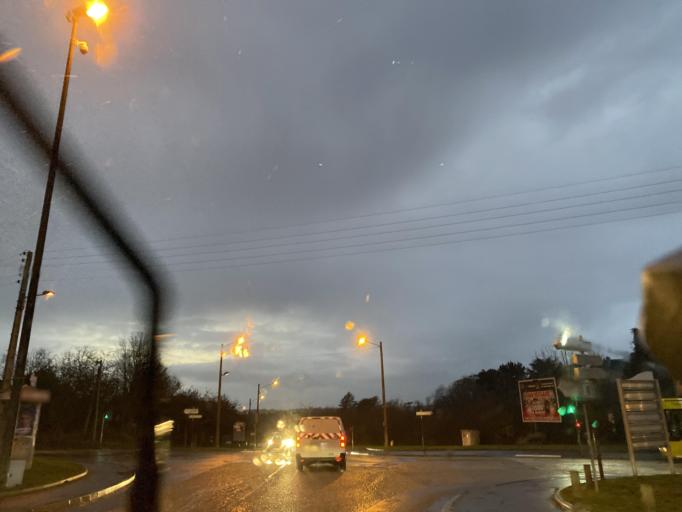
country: FR
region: Haute-Normandie
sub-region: Departement de l'Eure
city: Evreux
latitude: 49.0230
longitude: 1.1735
